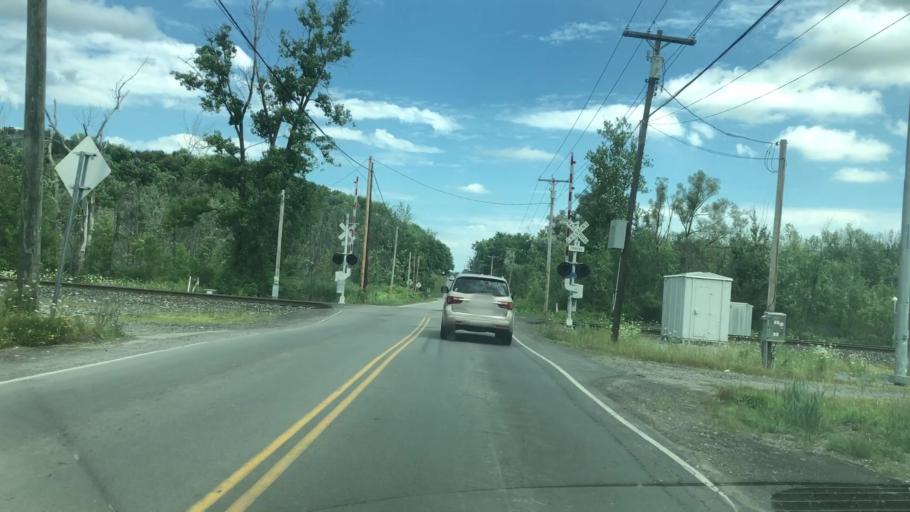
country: US
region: New York
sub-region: Wayne County
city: Macedon
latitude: 43.0765
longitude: -77.3613
